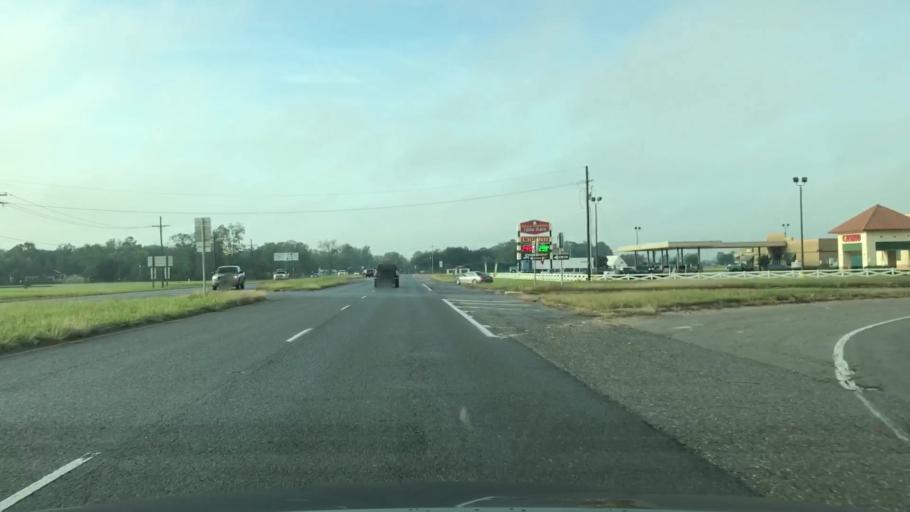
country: US
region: Louisiana
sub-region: Terrebonne Parish
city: Gray
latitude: 29.6799
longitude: -90.8125
